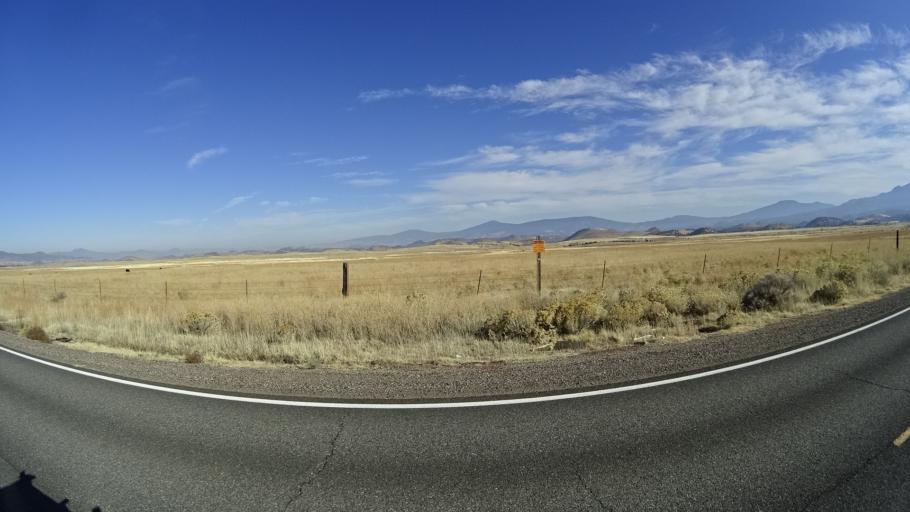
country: US
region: California
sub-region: Siskiyou County
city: Weed
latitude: 41.4780
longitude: -122.4902
